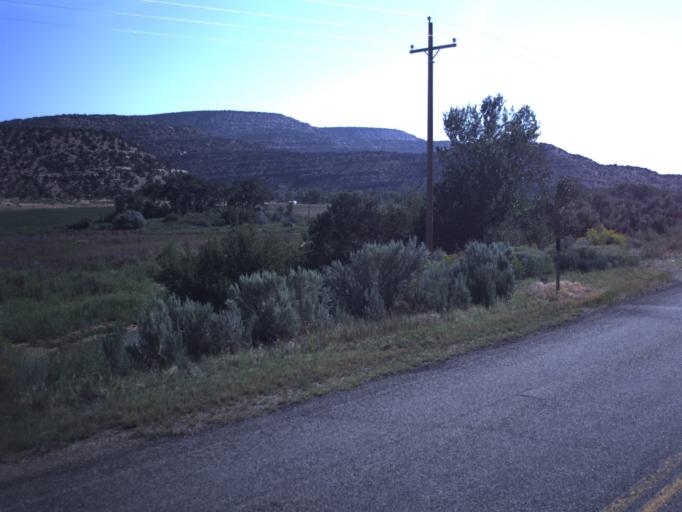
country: US
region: Utah
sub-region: Duchesne County
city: Duchesne
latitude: 40.2930
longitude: -110.5056
